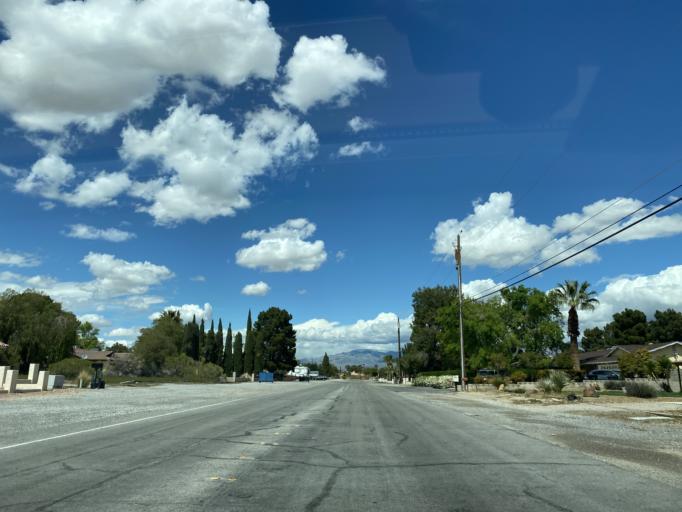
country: US
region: Nevada
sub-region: Clark County
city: Spring Valley
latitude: 36.2522
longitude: -115.2697
